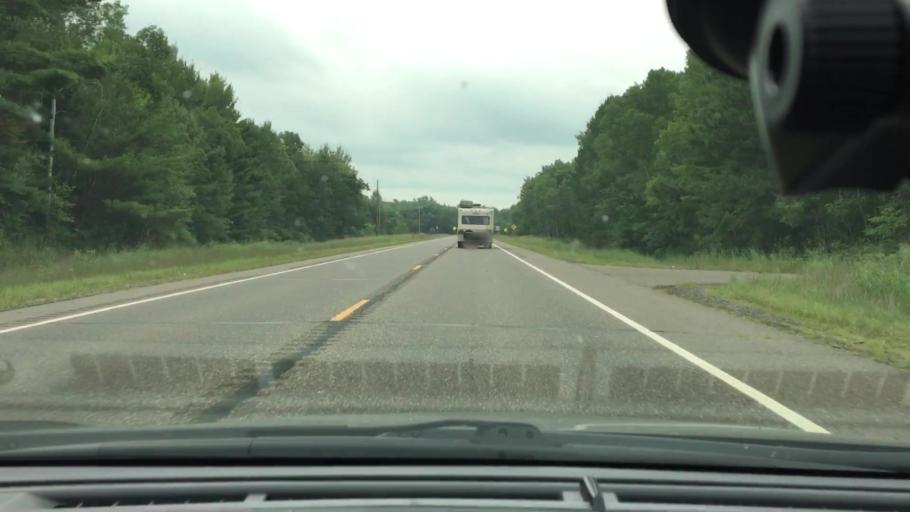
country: US
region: Minnesota
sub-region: Crow Wing County
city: Crosby
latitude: 46.4962
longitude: -93.9568
